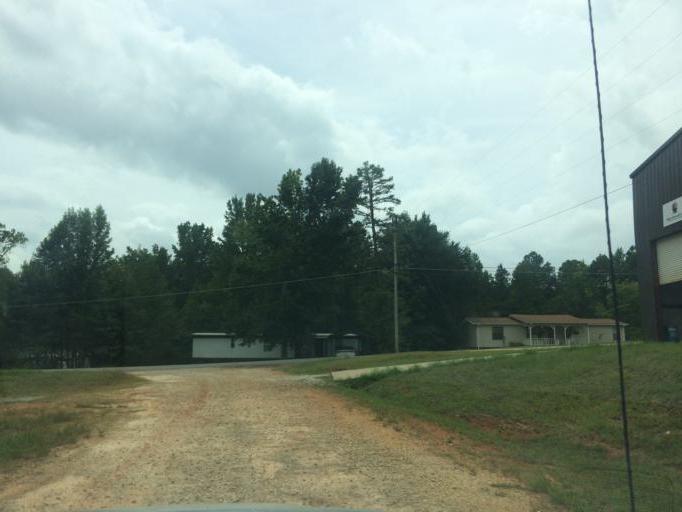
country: US
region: Georgia
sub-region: Elbert County
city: Elberton
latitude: 34.1299
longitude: -82.8628
